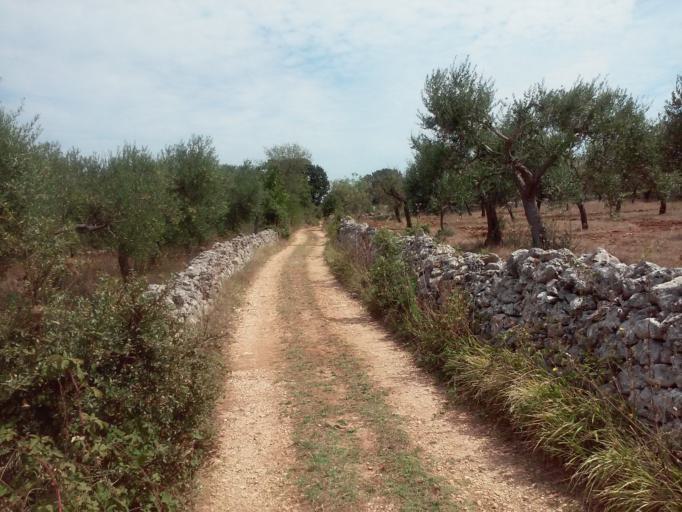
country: IT
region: Apulia
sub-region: Provincia di Bari
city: Gioia del Colle
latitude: 40.8216
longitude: 16.9661
